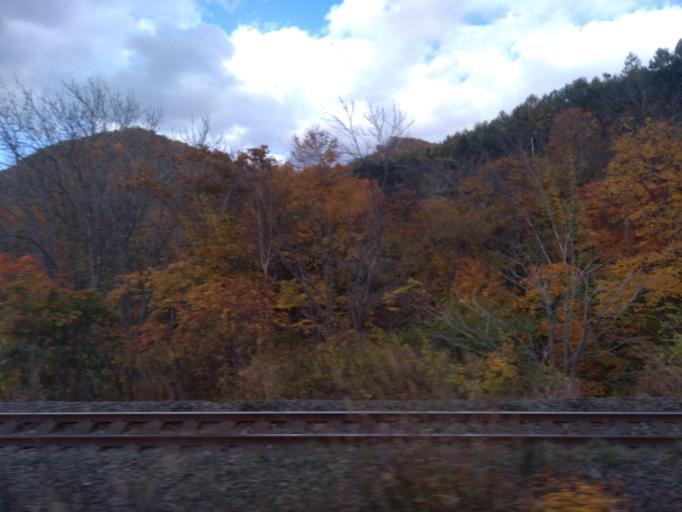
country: JP
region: Hokkaido
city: Niseko Town
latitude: 42.5955
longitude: 140.5880
